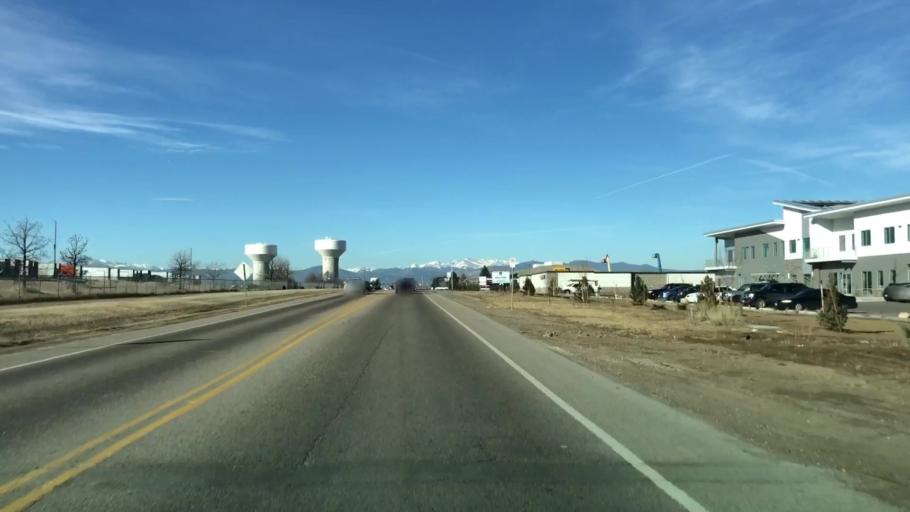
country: US
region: Colorado
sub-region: Weld County
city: Windsor
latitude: 40.4361
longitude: -104.9649
